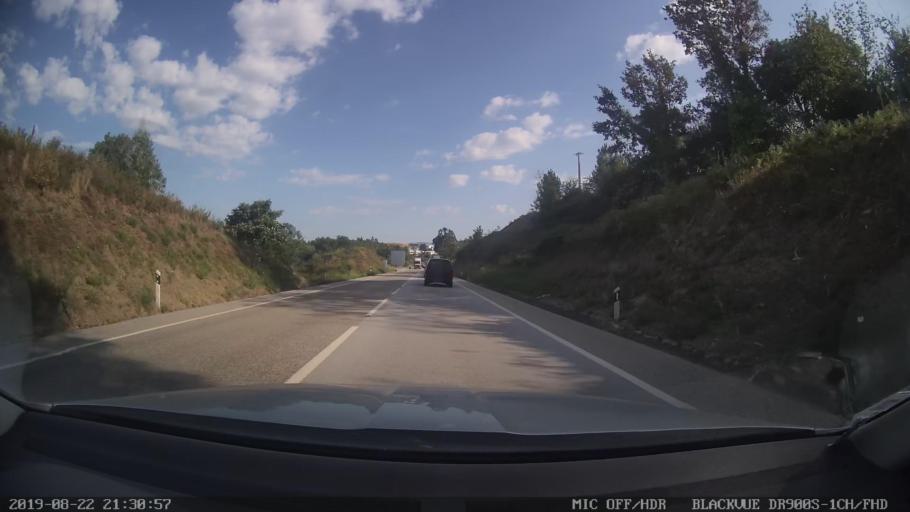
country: PT
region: Leiria
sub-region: Pedrogao Grande
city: Pedrogao Grande
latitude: 39.9147
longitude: -8.1536
